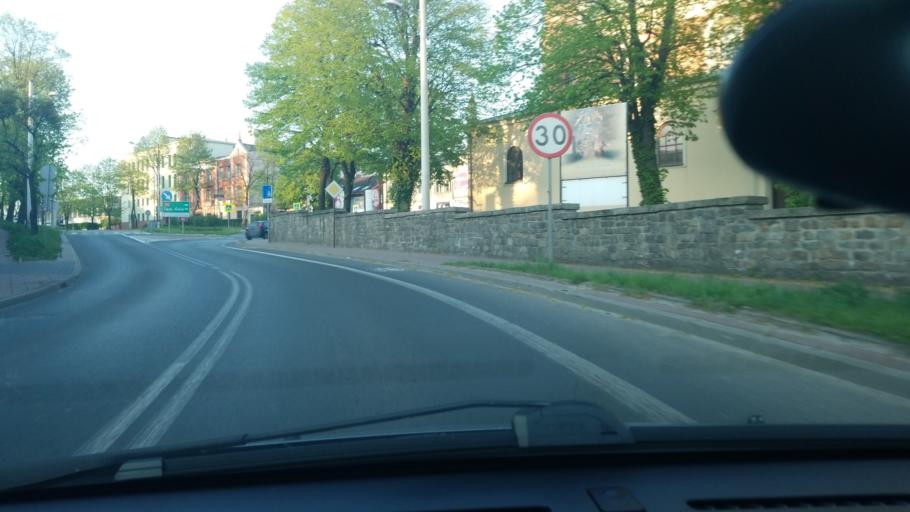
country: PL
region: Silesian Voivodeship
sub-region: Czestochowa
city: Czestochowa
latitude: 50.8046
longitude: 19.0939
